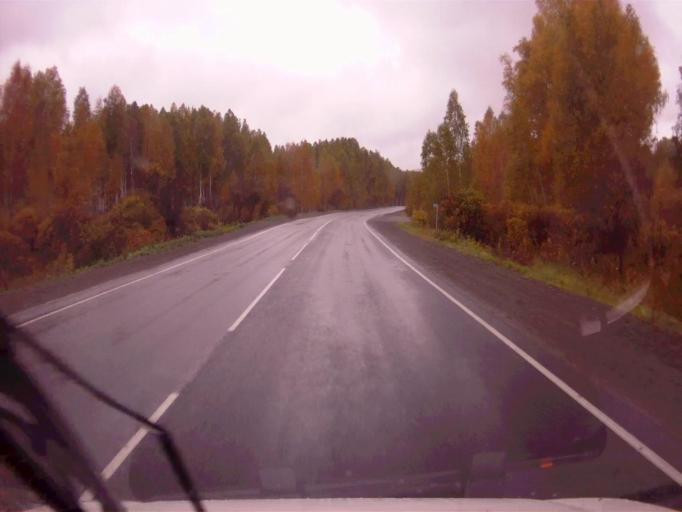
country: RU
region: Chelyabinsk
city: Argayash
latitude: 55.4782
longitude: 60.7674
